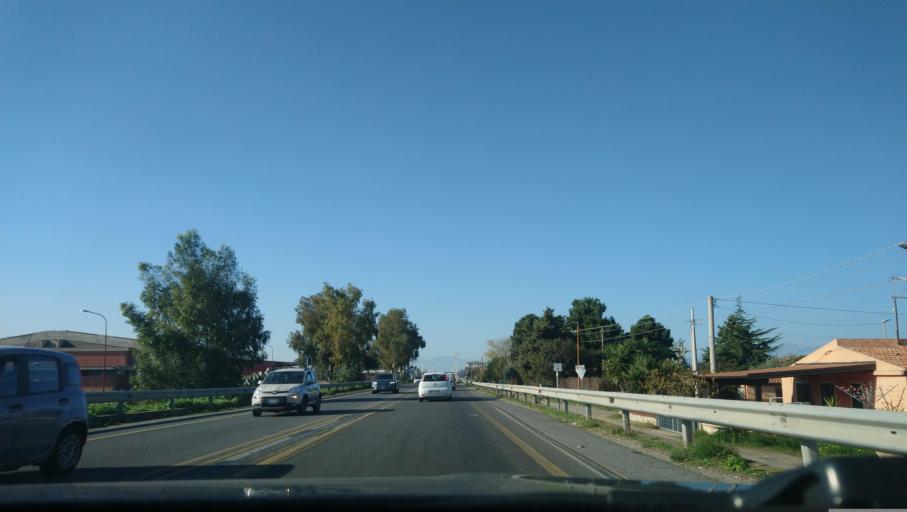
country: IT
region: Calabria
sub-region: Provincia di Cosenza
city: Fabrizio
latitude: 39.6313
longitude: 16.5686
